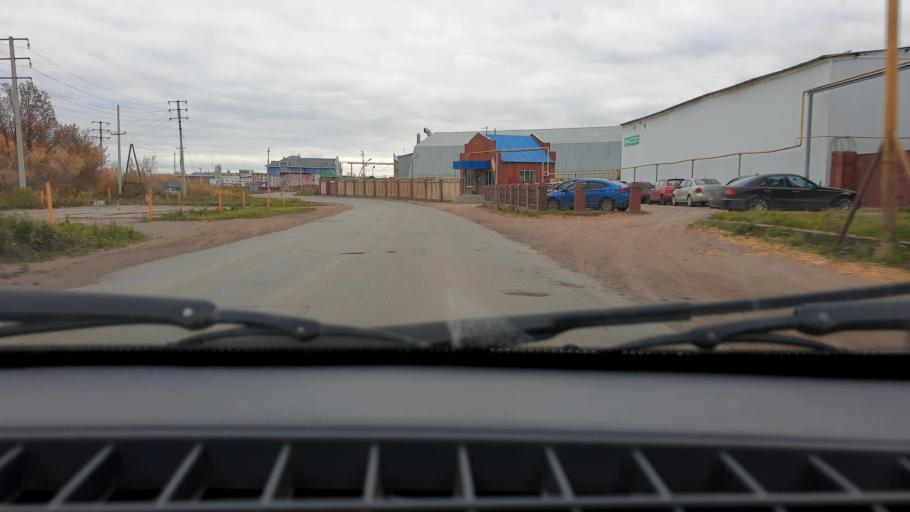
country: RU
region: Bashkortostan
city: Ufa
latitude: 54.5740
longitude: 55.9204
